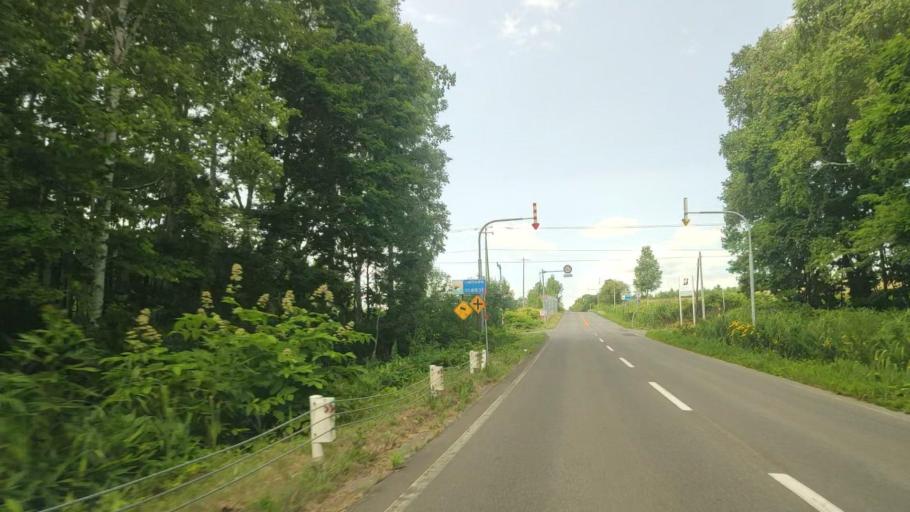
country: JP
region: Hokkaido
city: Nayoro
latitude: 44.2456
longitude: 142.4156
